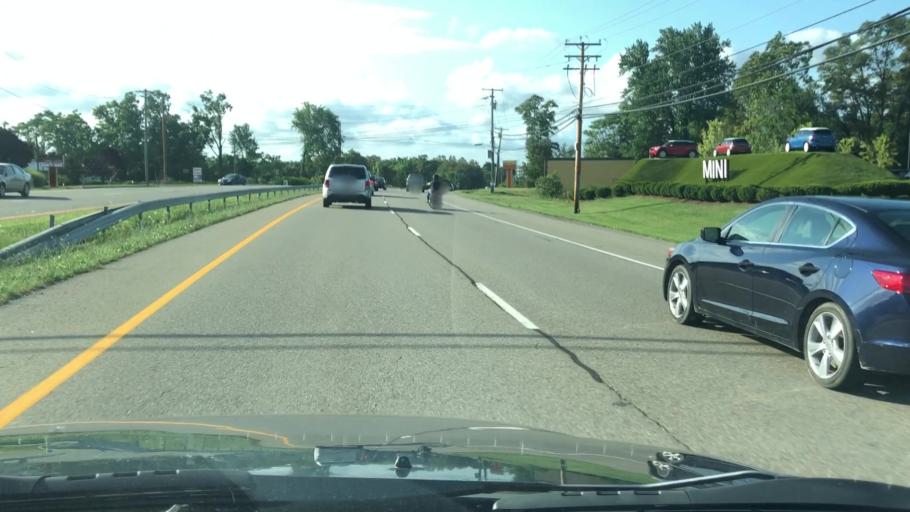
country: US
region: New York
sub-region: Dutchess County
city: Wappingers Falls
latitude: 41.5674
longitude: -73.9077
